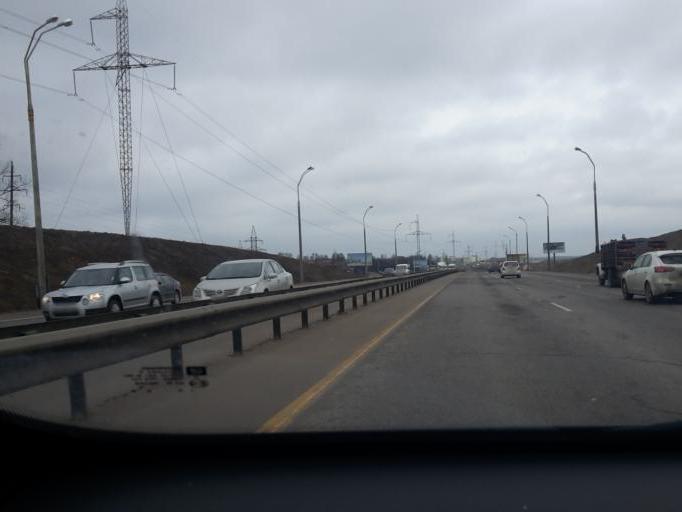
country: BY
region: Minsk
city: Zhdanovichy
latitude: 53.9211
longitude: 27.4145
